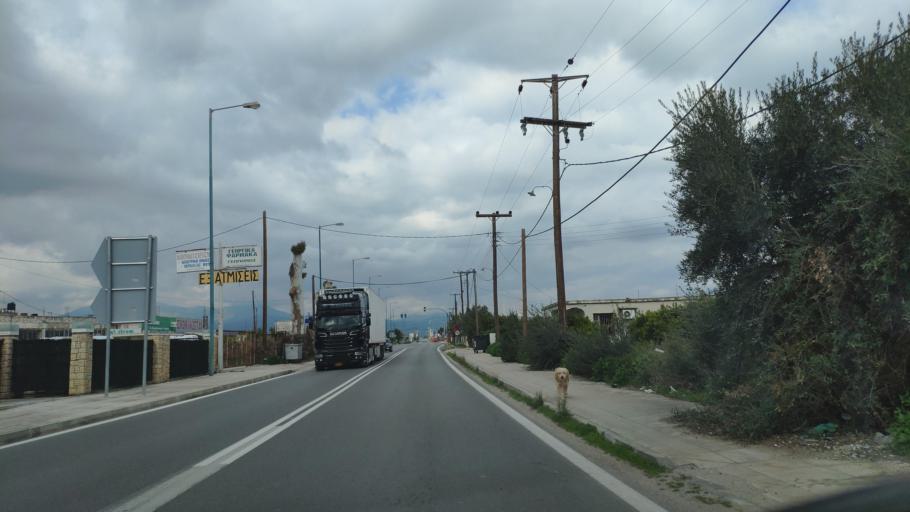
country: GR
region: Peloponnese
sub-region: Nomos Argolidos
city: Argos
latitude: 37.6512
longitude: 22.7286
